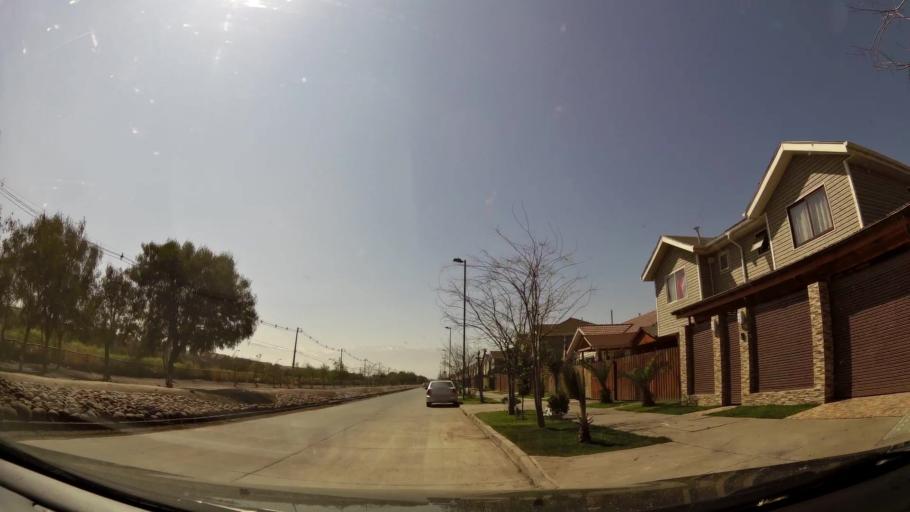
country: CL
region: Santiago Metropolitan
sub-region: Provincia de Chacabuco
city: Chicureo Abajo
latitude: -33.3270
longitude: -70.7531
